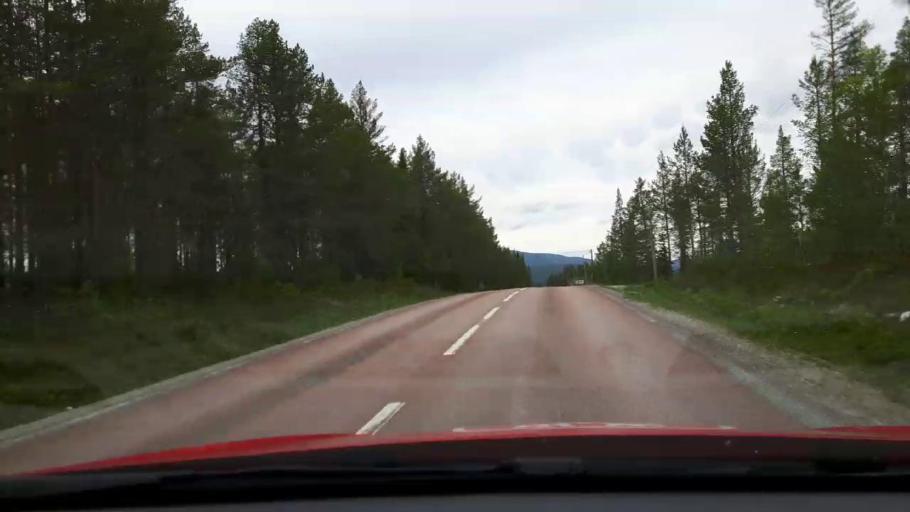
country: NO
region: Hedmark
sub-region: Engerdal
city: Engerdal
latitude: 62.4983
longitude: 12.6305
